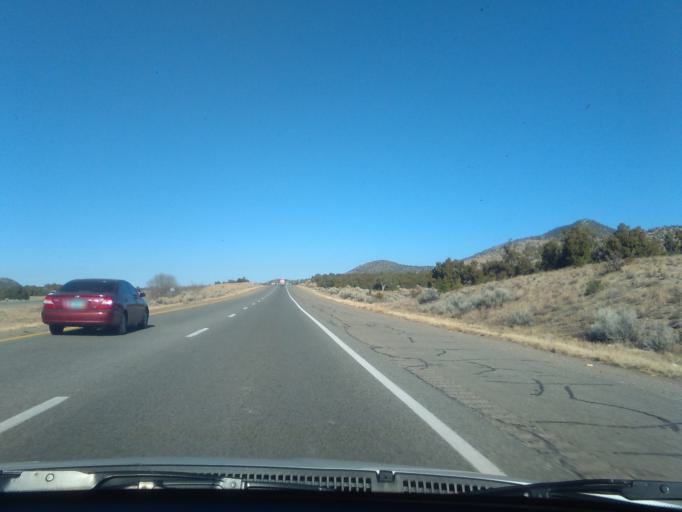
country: US
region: New Mexico
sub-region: Santa Fe County
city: Eldorado at Santa Fe
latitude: 35.5608
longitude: -105.8826
